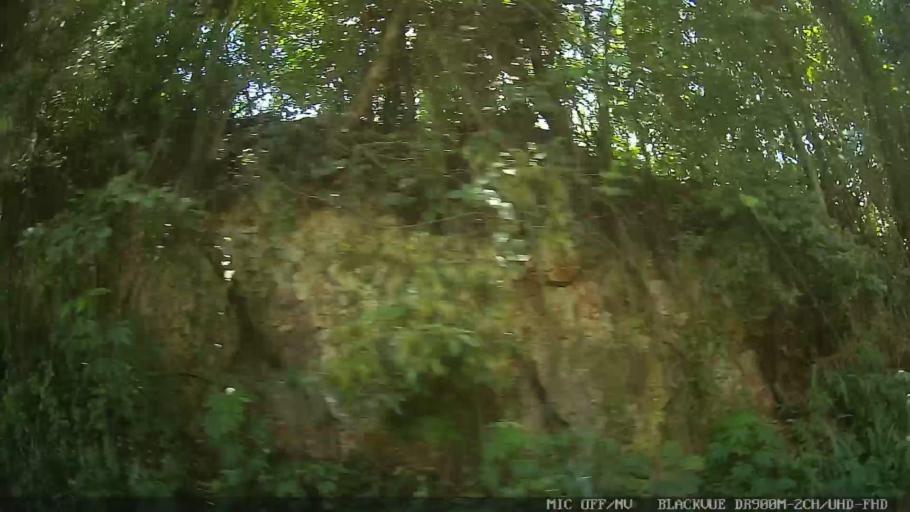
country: BR
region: Sao Paulo
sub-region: Laranjal Paulista
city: Laranjal Paulista
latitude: -23.0275
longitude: -47.8434
